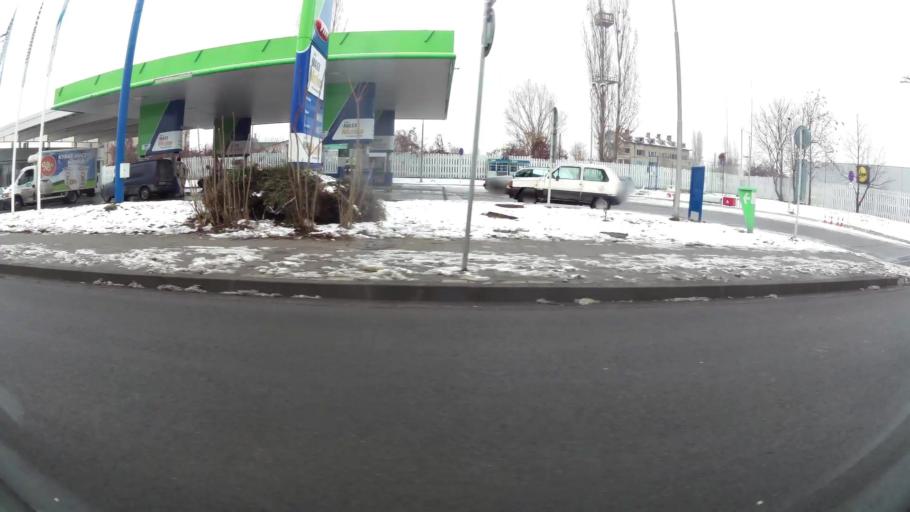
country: BG
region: Sofia-Capital
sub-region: Stolichna Obshtina
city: Sofia
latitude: 42.7079
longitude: 23.3421
